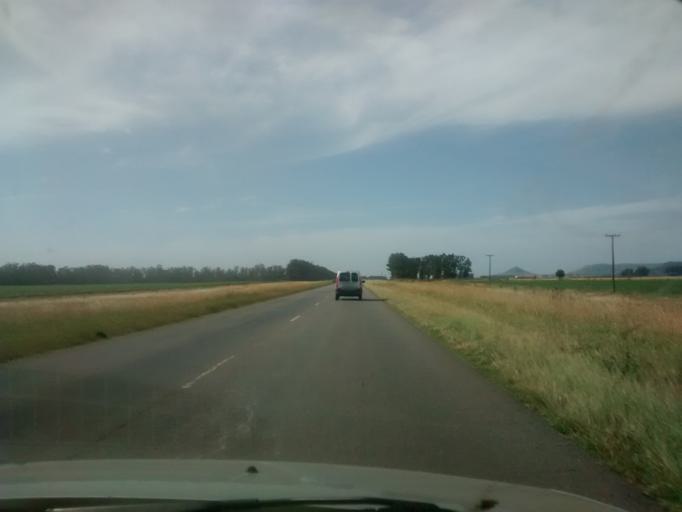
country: AR
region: Buenos Aires
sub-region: Partido de Loberia
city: Loberia
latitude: -37.9503
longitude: -58.6899
